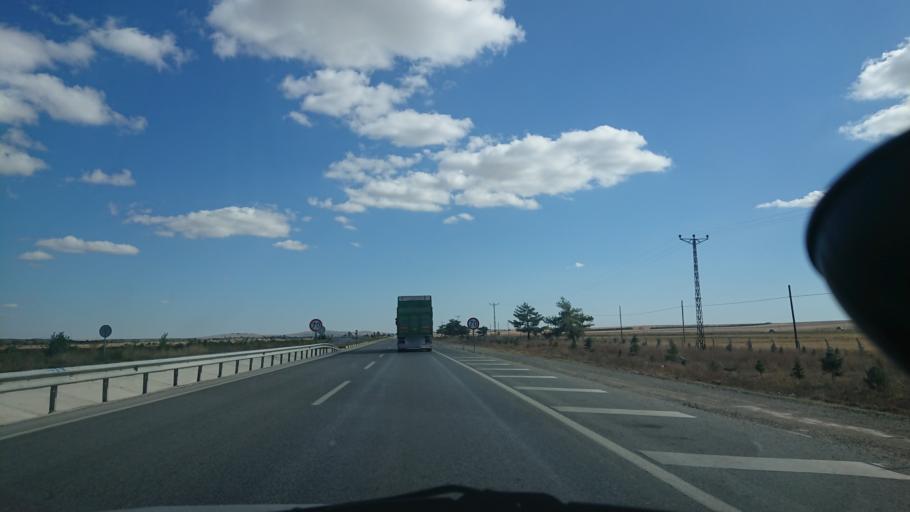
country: TR
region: Eskisehir
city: Mahmudiye
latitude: 39.5580
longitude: 30.9185
